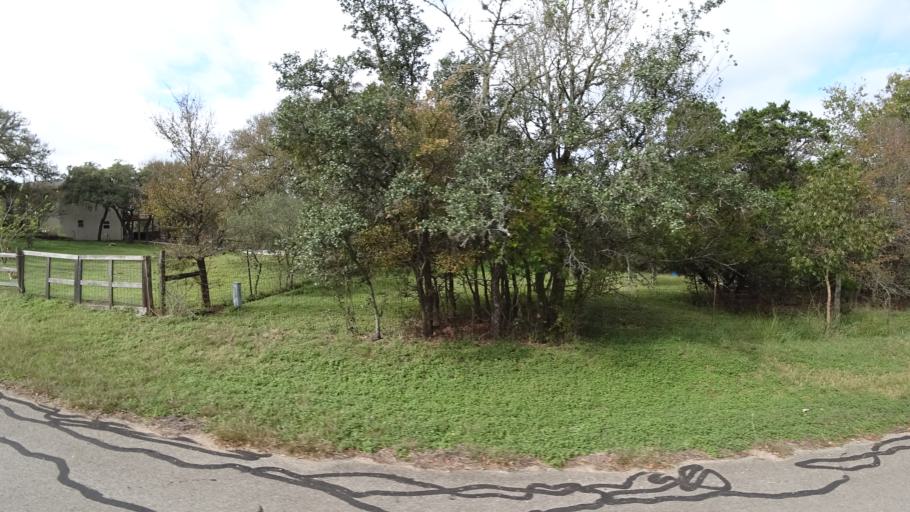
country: US
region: Texas
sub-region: Travis County
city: Shady Hollow
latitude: 30.1340
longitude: -97.8915
